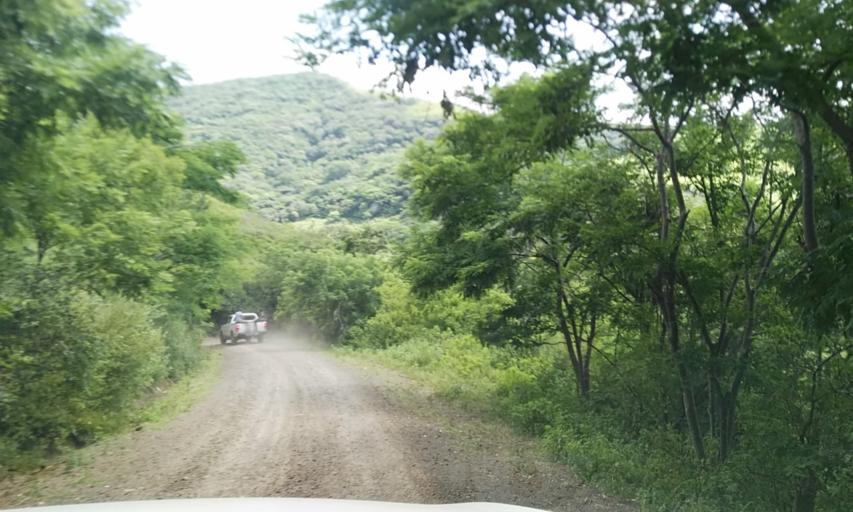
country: NI
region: Matagalpa
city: Terrabona
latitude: 12.6988
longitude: -85.9373
